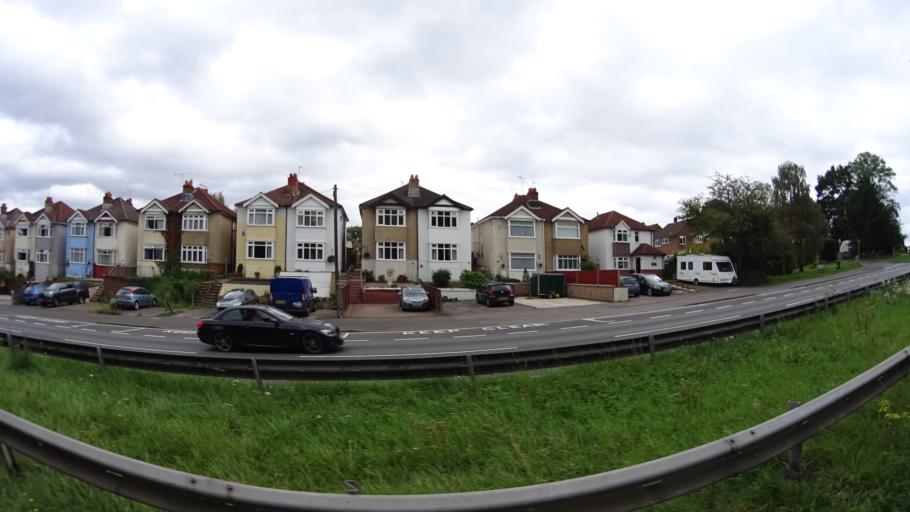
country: GB
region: England
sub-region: Hampshire
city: Totton
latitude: 50.9112
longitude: -1.4946
